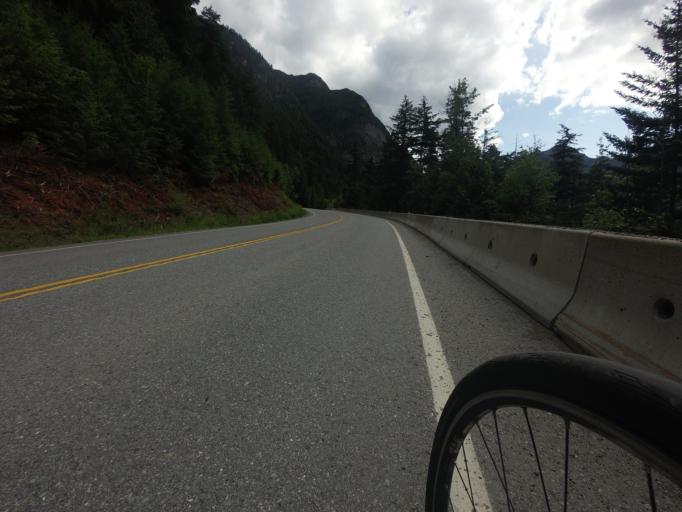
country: CA
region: British Columbia
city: Lillooet
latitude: 50.6334
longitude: -122.0890
